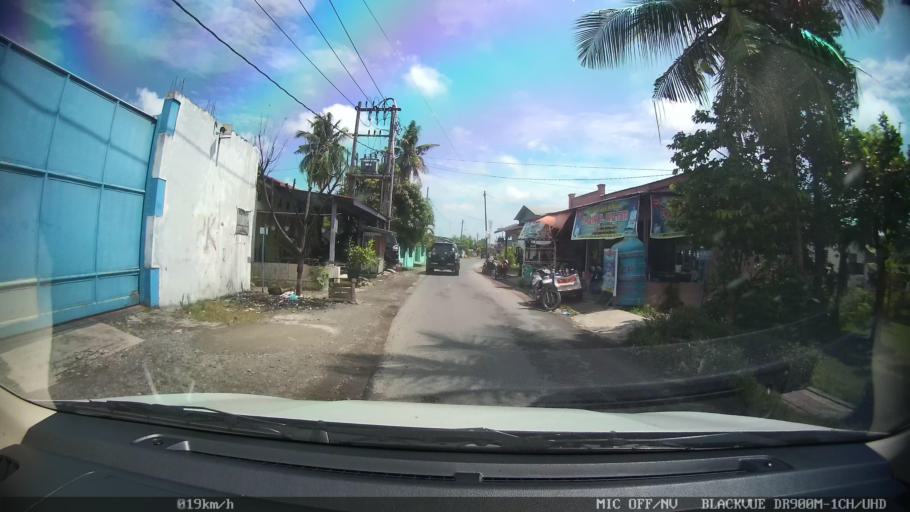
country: ID
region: North Sumatra
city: Medan
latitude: 3.6012
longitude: 98.7487
